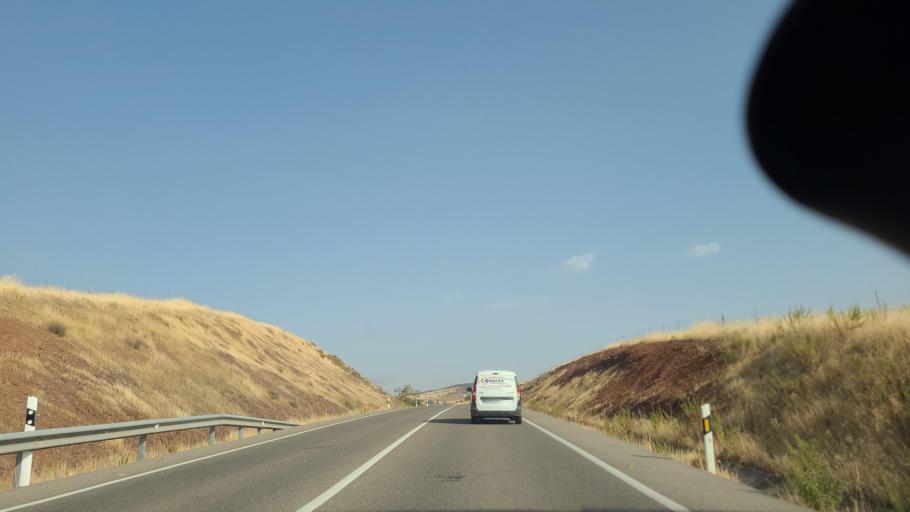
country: ES
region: Andalusia
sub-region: Province of Cordoba
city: Penarroya-Pueblonuevo
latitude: 38.3039
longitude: -5.2567
